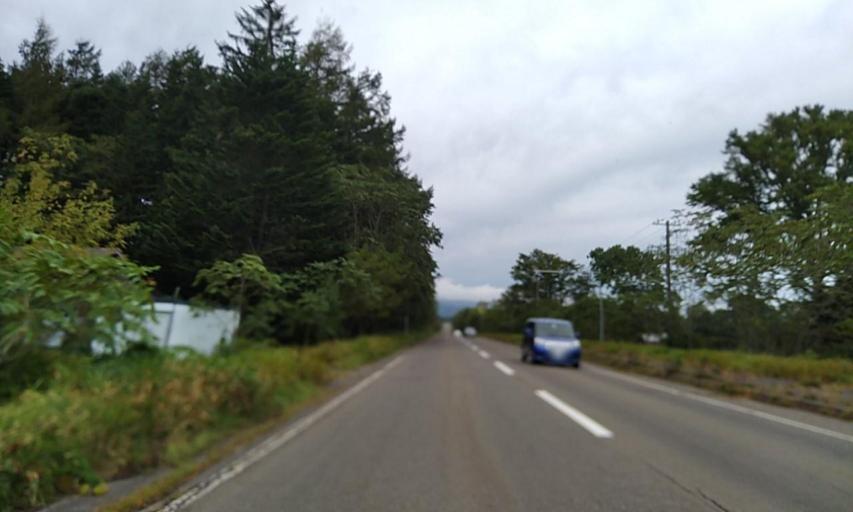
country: JP
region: Hokkaido
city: Bihoro
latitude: 43.5548
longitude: 144.3301
